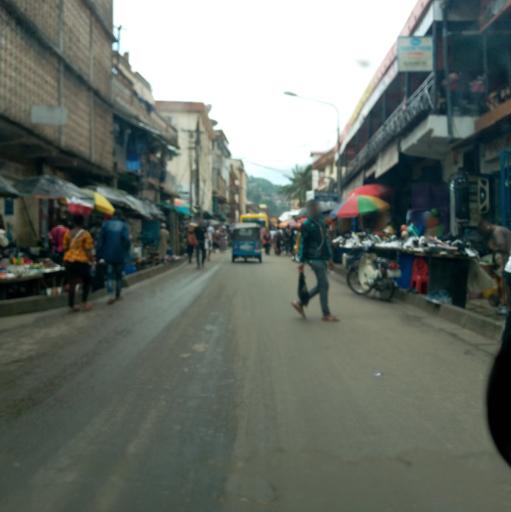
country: SL
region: Western Area
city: Freetown
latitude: 8.4874
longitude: -13.2308
